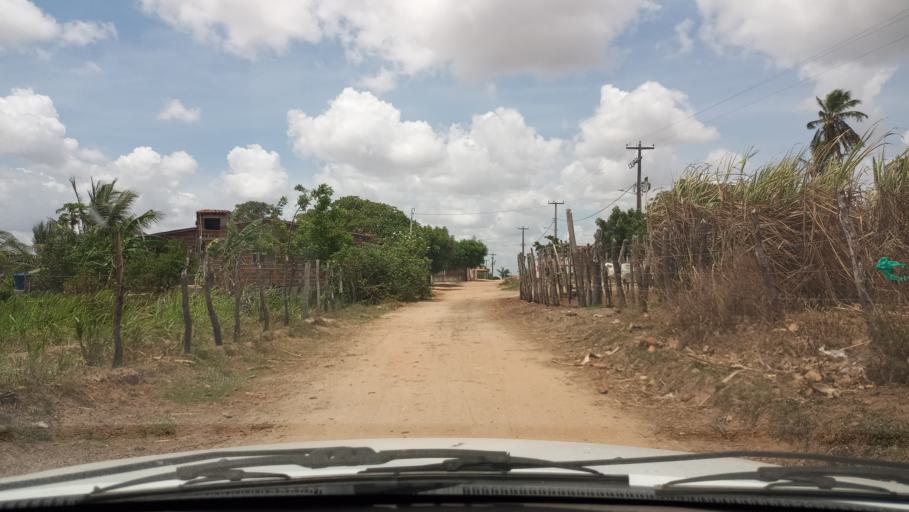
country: BR
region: Rio Grande do Norte
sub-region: Brejinho
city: Brejinho
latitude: -6.2858
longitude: -35.3536
